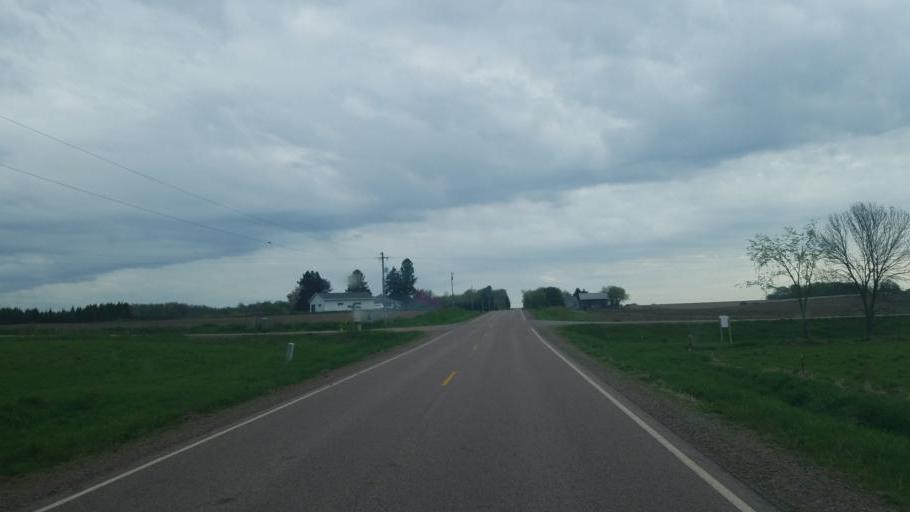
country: US
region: Wisconsin
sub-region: Wood County
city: Marshfield
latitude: 44.5841
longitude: -90.2994
